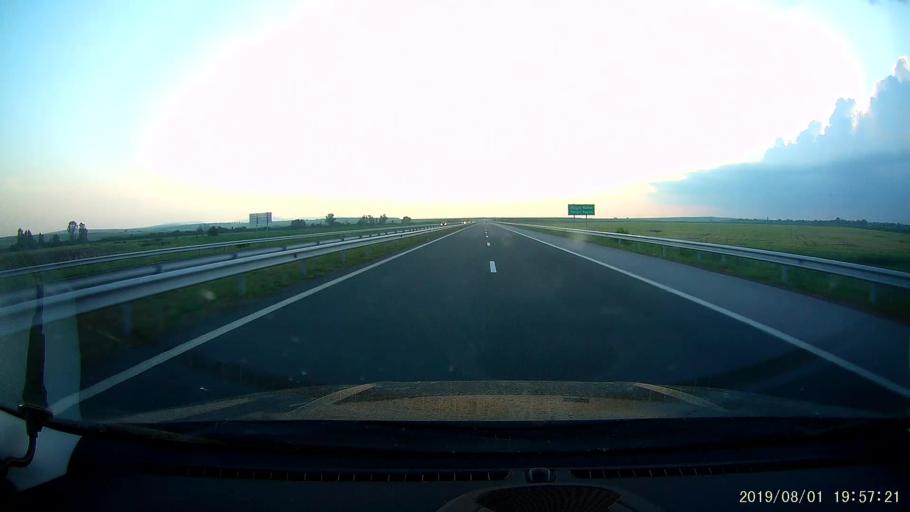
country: BG
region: Yambol
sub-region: Obshtina Straldzha
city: Straldzha
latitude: 42.5534
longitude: 26.8017
